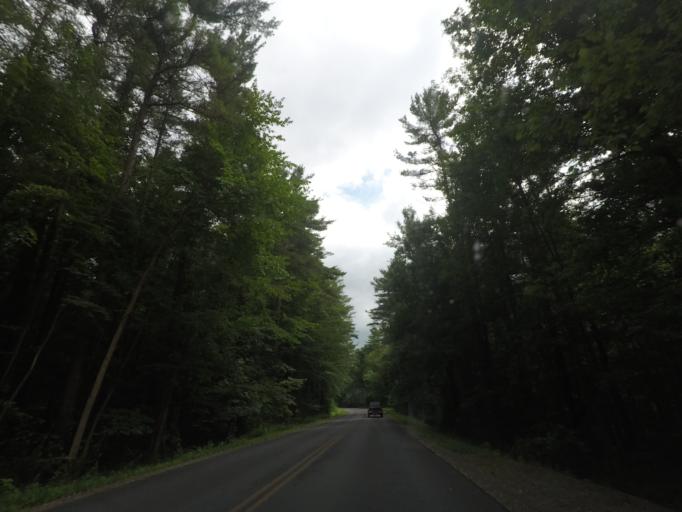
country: US
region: New York
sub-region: Saratoga County
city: Stillwater
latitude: 42.8614
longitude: -73.5562
